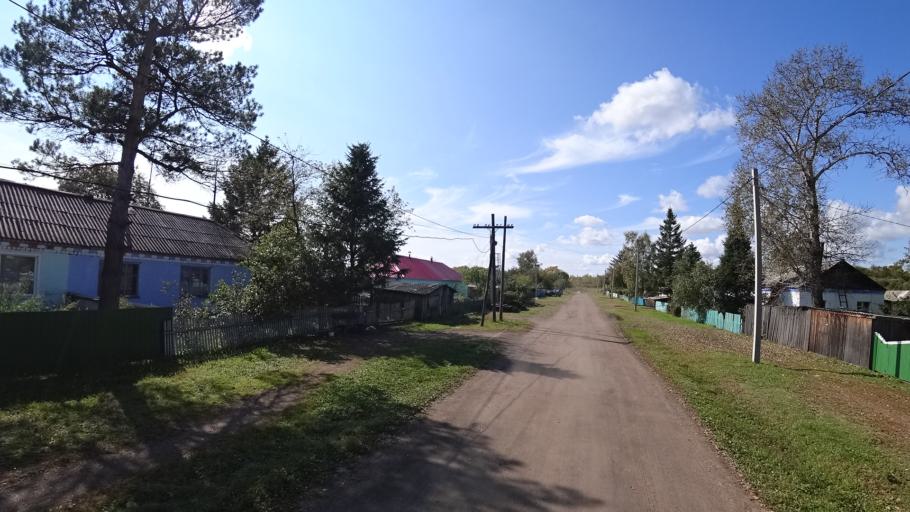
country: RU
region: Amur
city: Arkhara
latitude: 49.4050
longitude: 130.1346
